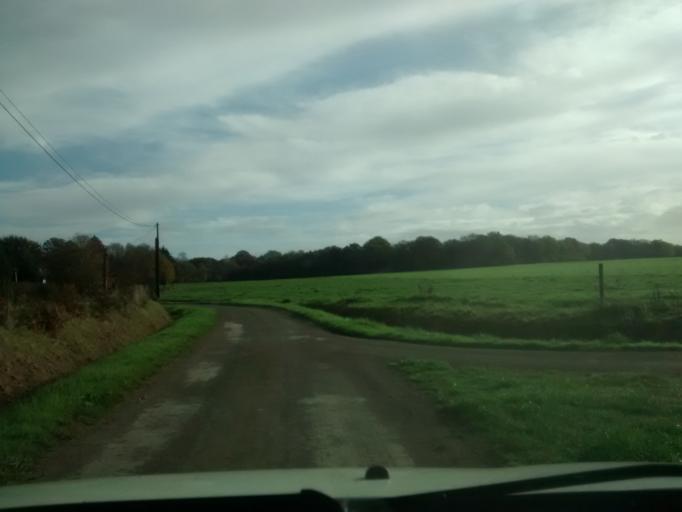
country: FR
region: Brittany
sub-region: Departement d'Ille-et-Vilaine
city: Servon-sur-Vilaine
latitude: 48.1409
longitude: -1.4706
